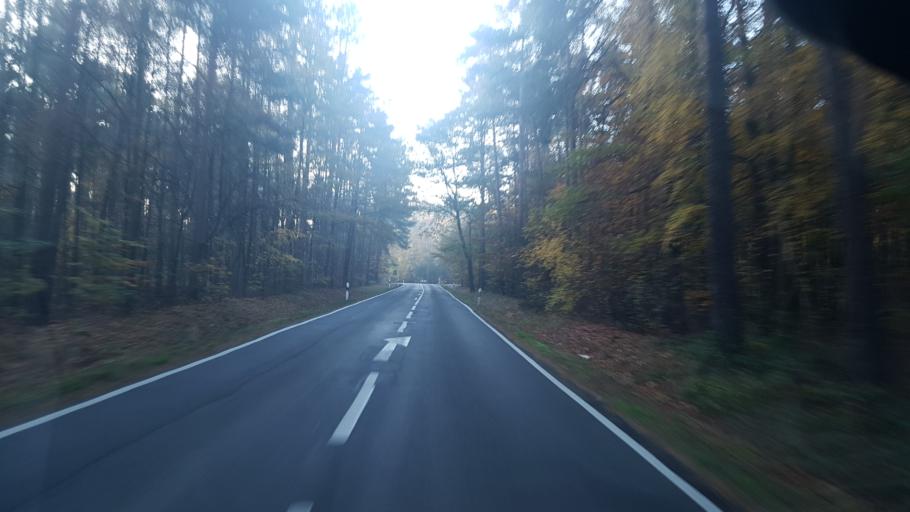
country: DE
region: Saxony
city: Dahlen
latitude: 51.4110
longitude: 12.9723
